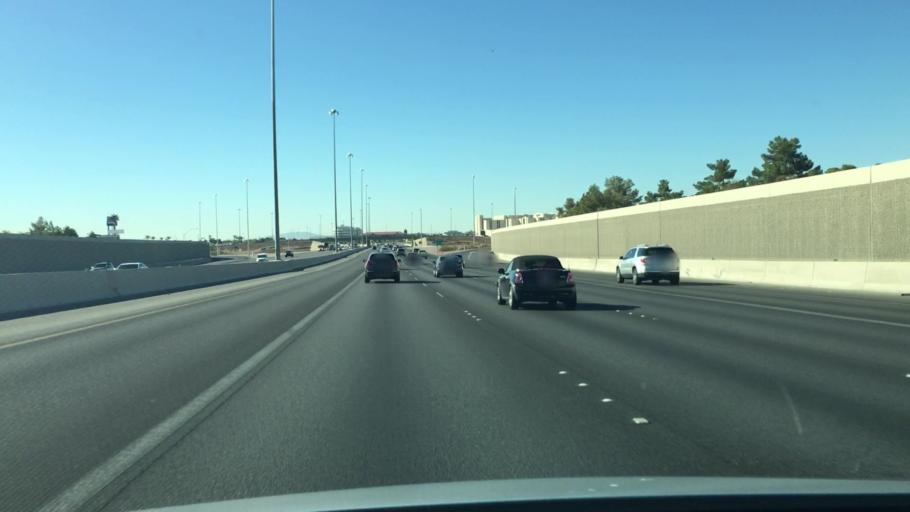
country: US
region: Nevada
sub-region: Clark County
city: Spring Valley
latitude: 36.2241
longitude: -115.2473
